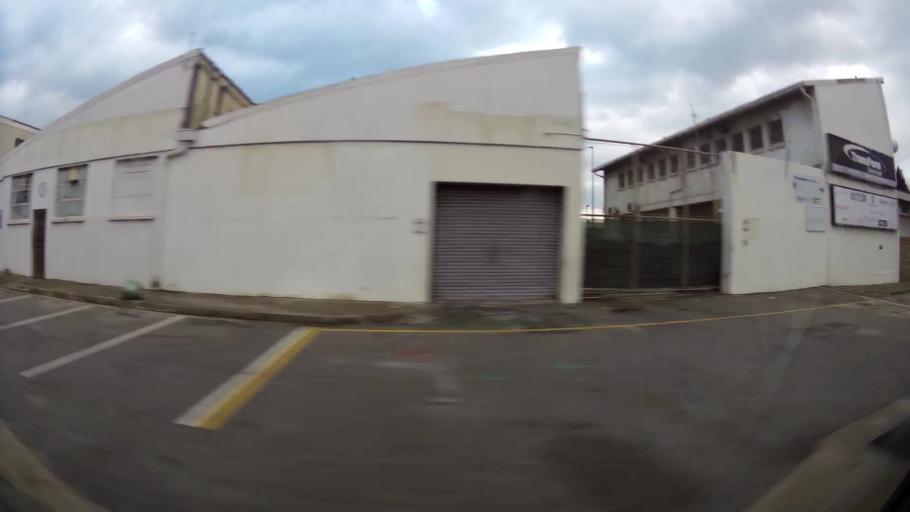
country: ZA
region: Eastern Cape
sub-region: Nelson Mandela Bay Metropolitan Municipality
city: Port Elizabeth
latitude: -33.9345
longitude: 25.6094
